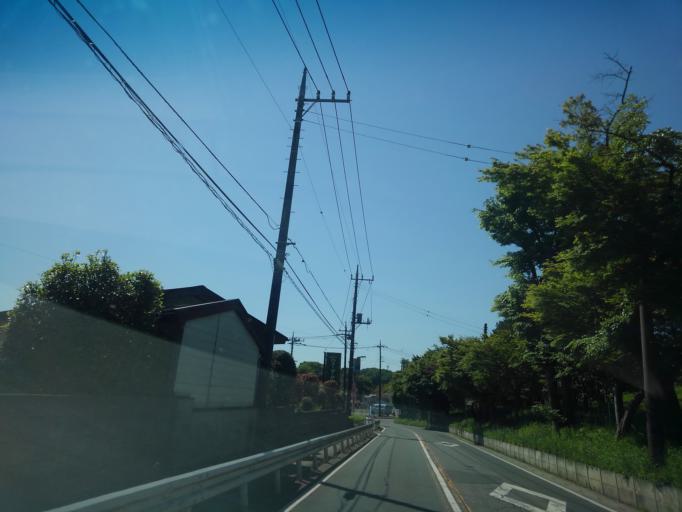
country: JP
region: Saitama
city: Tokorozawa
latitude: 35.7786
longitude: 139.4174
